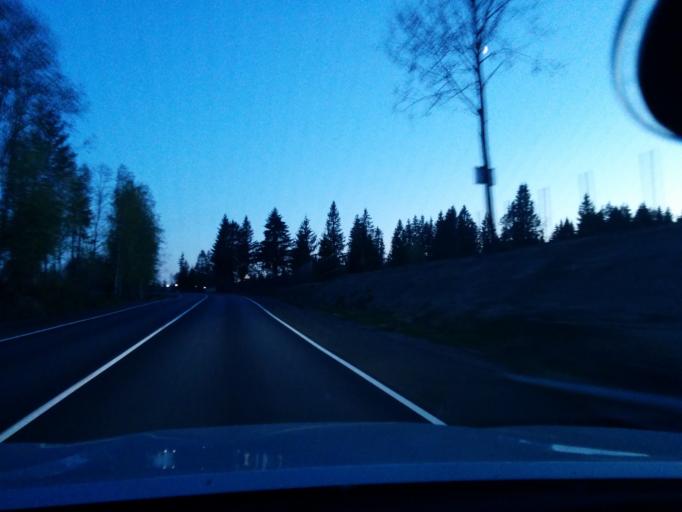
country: RU
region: Leningrad
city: Verkhniye Osel'ki
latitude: 60.1822
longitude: 30.3865
